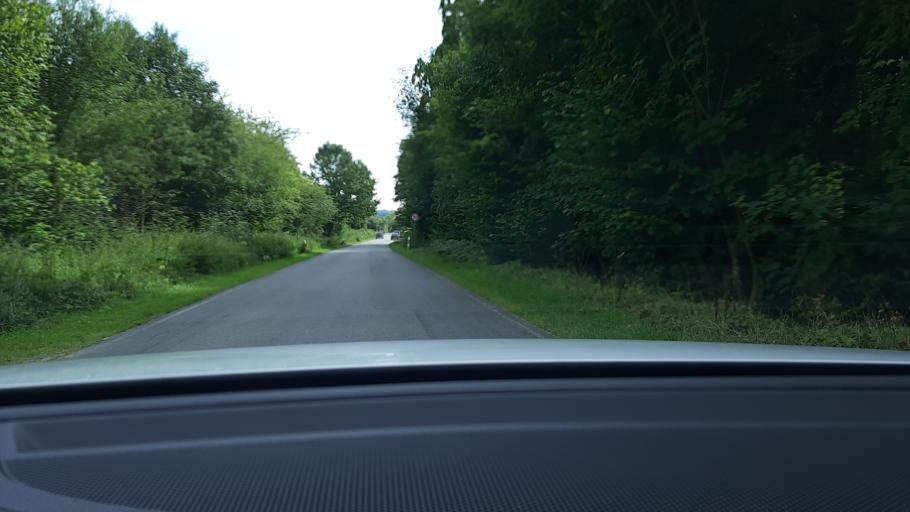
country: DE
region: Schleswig-Holstein
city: Reinfeld
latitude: 53.8436
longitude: 10.4710
